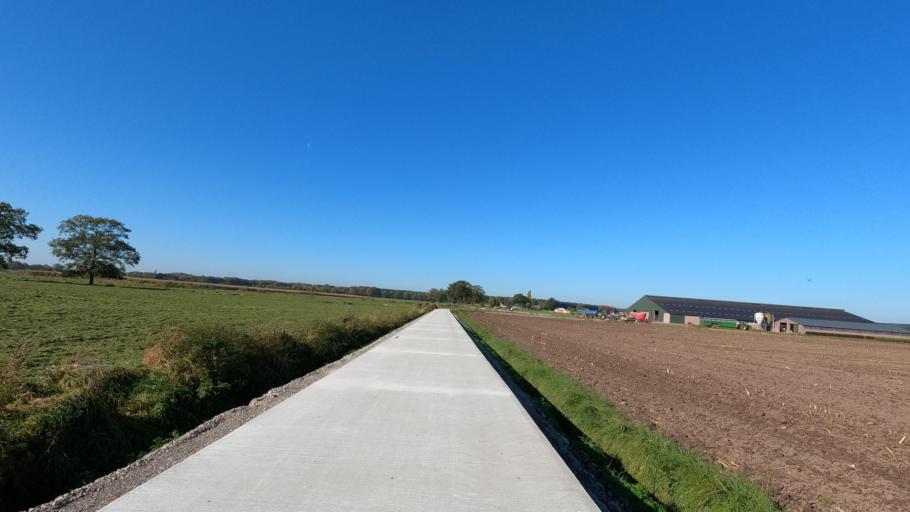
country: BE
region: Flanders
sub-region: Provincie Antwerpen
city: Merksplas
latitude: 51.3447
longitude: 4.8538
